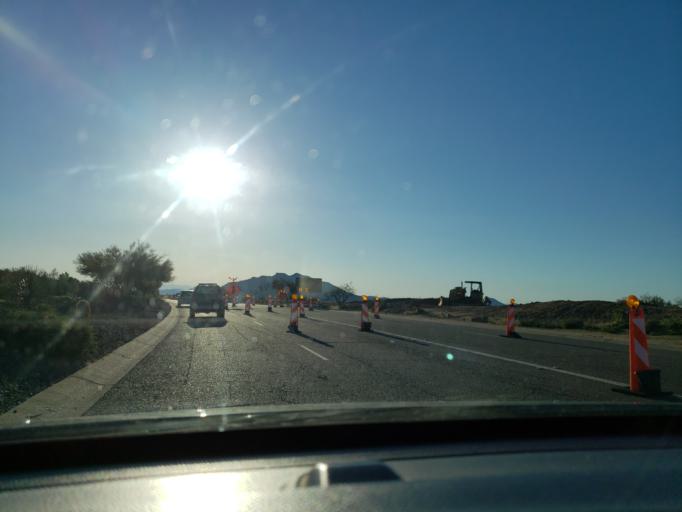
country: US
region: Arizona
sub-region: Maricopa County
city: Carefree
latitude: 33.8248
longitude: -111.8769
